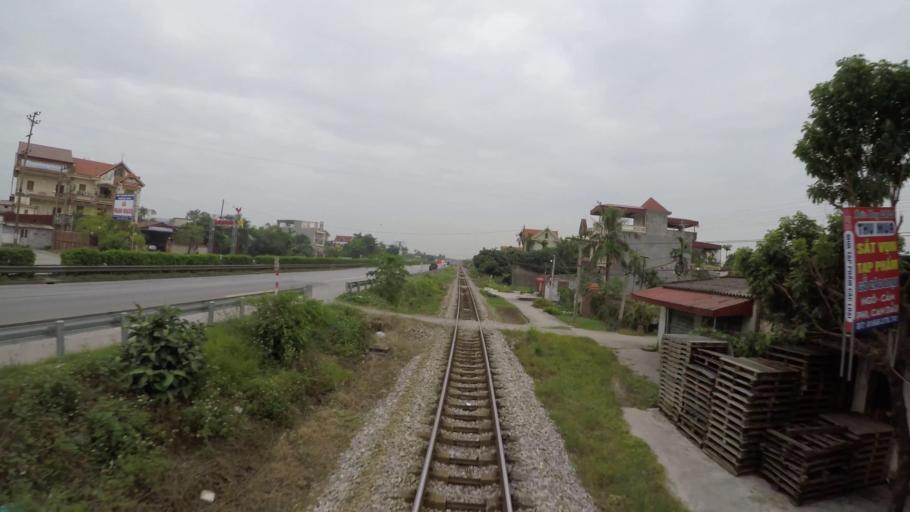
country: VN
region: Hai Duong
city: Phu Thai
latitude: 20.9715
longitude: 106.4418
